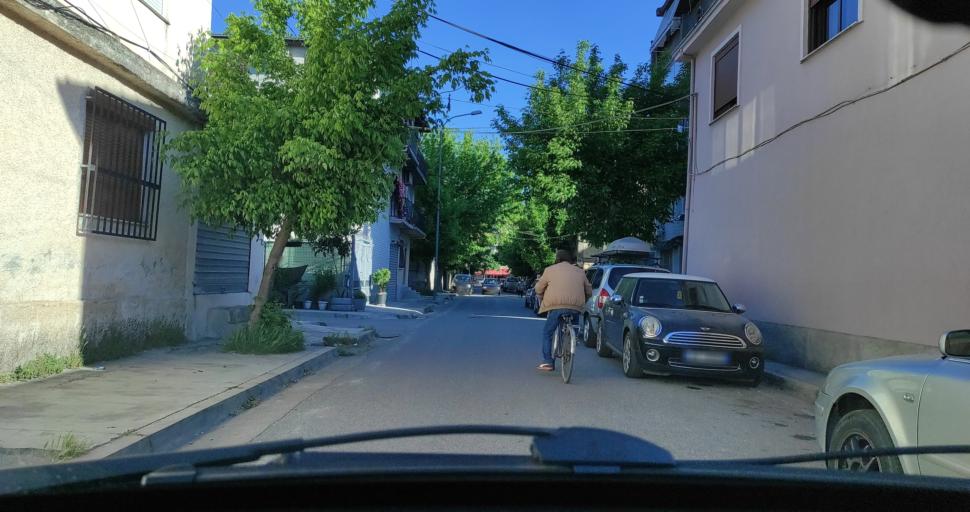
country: AL
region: Shkoder
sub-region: Rrethi i Shkodres
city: Shkoder
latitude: 42.0590
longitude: 19.5105
